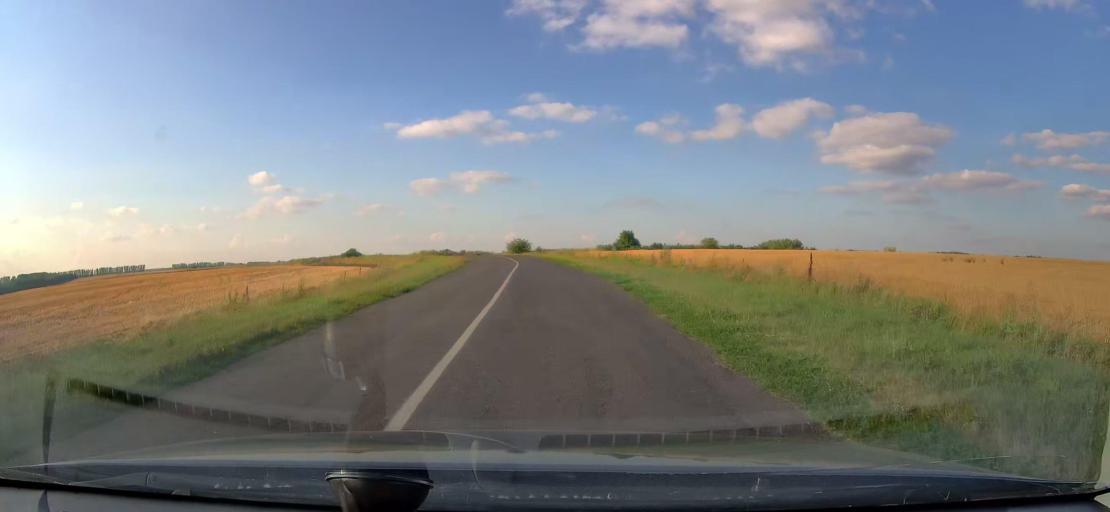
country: RU
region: Kursk
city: Zolotukhino
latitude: 52.0324
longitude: 36.2174
